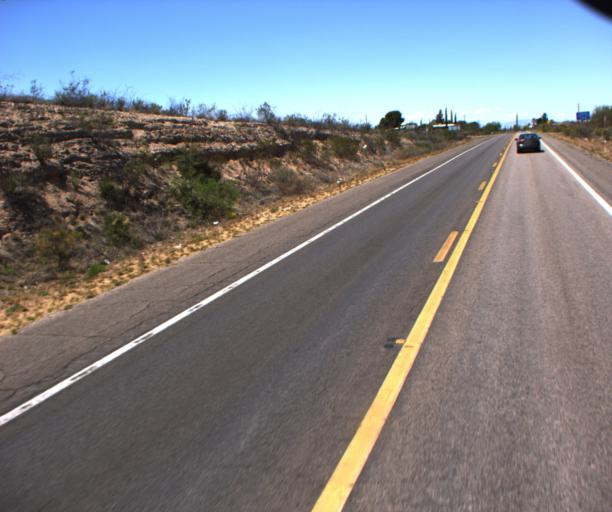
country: US
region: Arizona
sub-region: Cochise County
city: Tombstone
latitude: 31.7056
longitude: -110.0523
